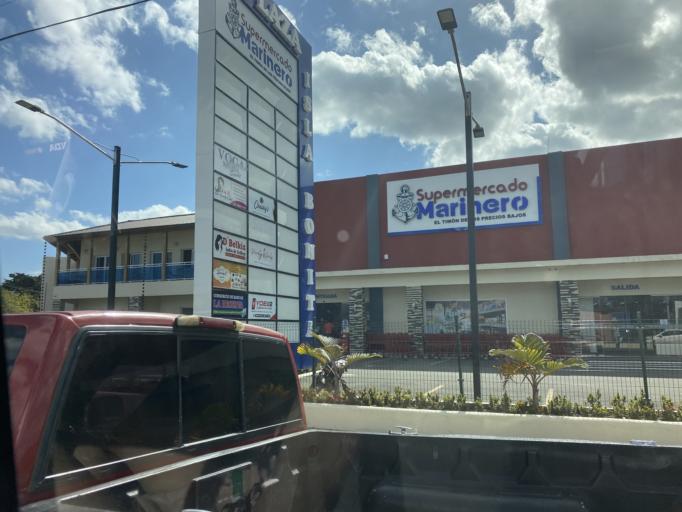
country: DO
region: Espaillat
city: Jamao al Norte
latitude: 19.6696
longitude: -70.3693
